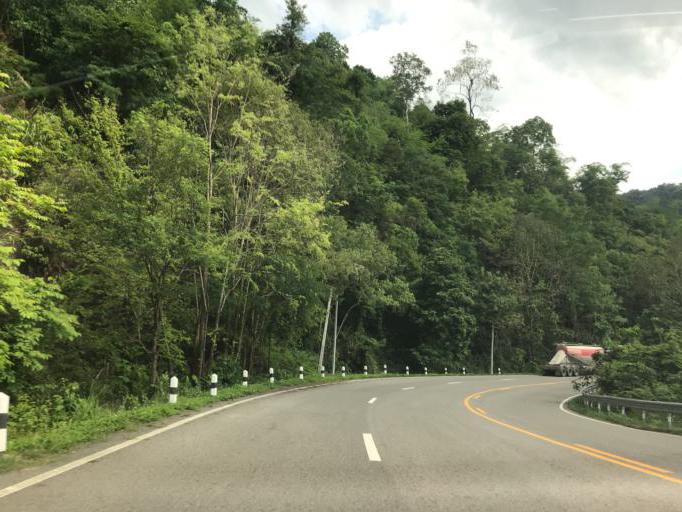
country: TH
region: Phayao
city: Phayao
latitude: 19.0671
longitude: 99.8086
